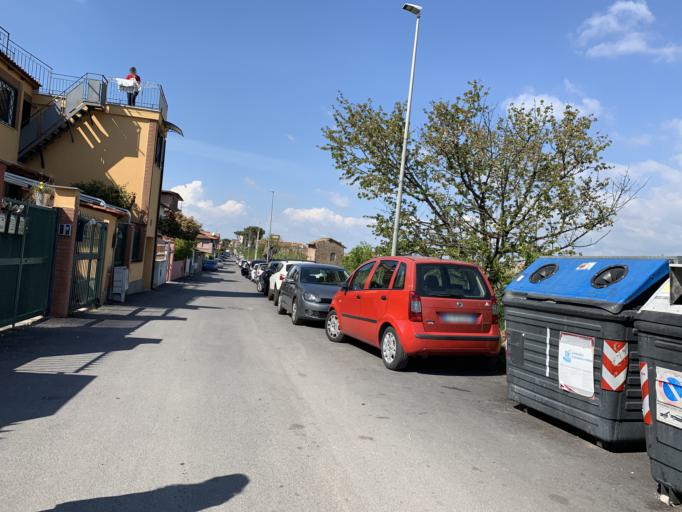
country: IT
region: Latium
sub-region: Citta metropolitana di Roma Capitale
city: Rome
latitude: 41.8604
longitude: 12.5440
